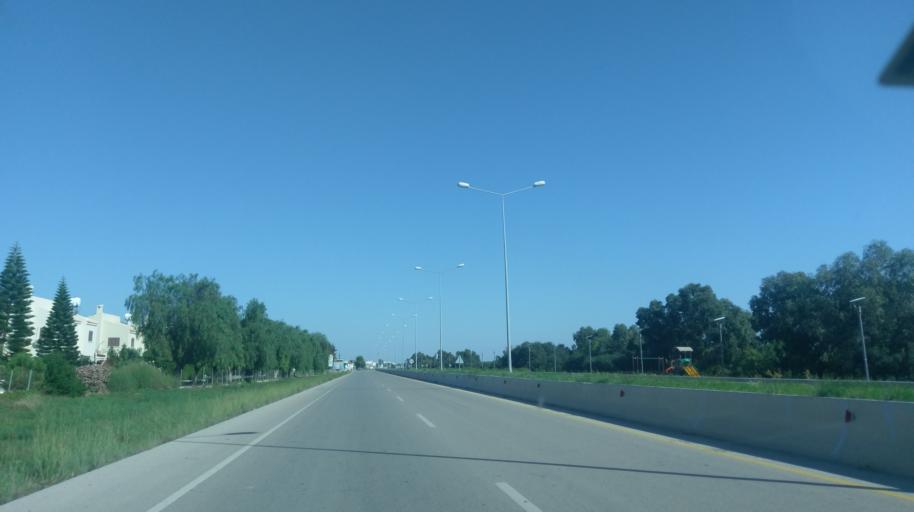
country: CY
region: Ammochostos
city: Trikomo
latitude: 35.2754
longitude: 33.9177
